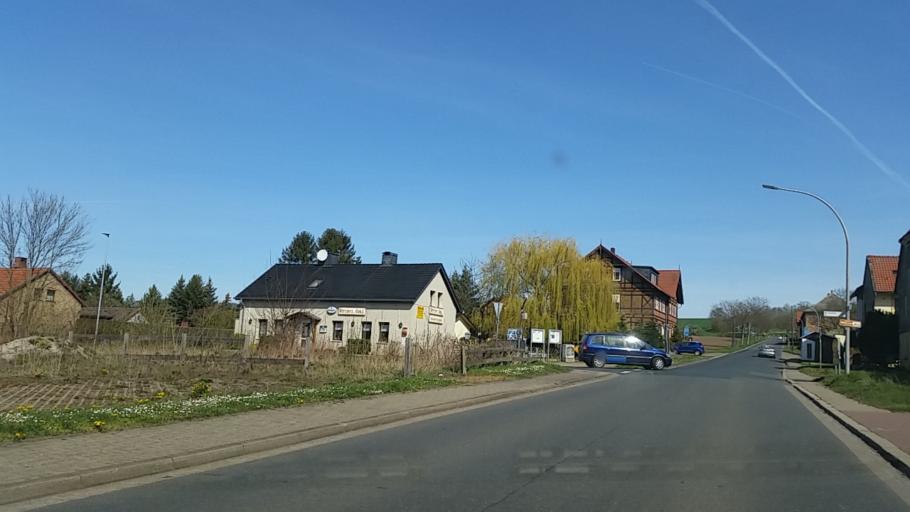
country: DE
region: Lower Saxony
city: Jerxheim
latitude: 52.0663
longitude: 10.8913
